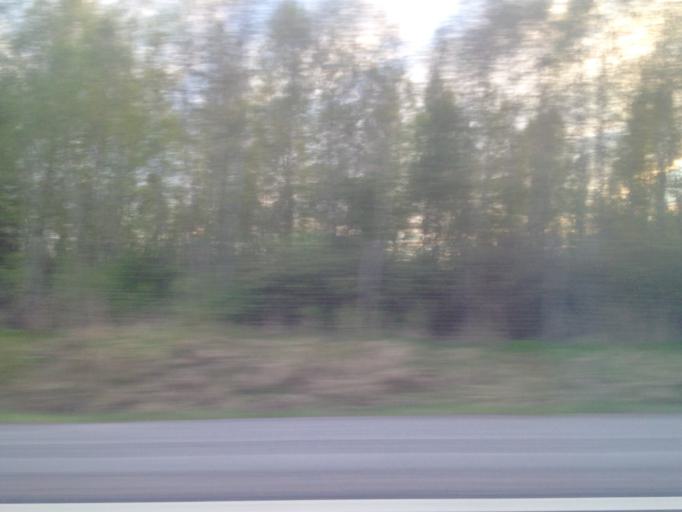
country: FI
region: Haeme
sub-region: Riihimaeki
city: Riihimaeki
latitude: 60.7071
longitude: 24.7371
